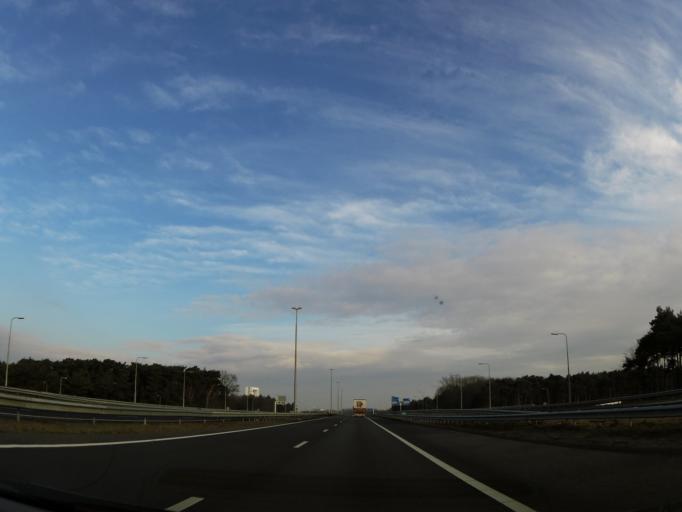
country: NL
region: Limburg
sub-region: Gemeente Venlo
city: Venlo
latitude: 51.3926
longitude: 6.1281
